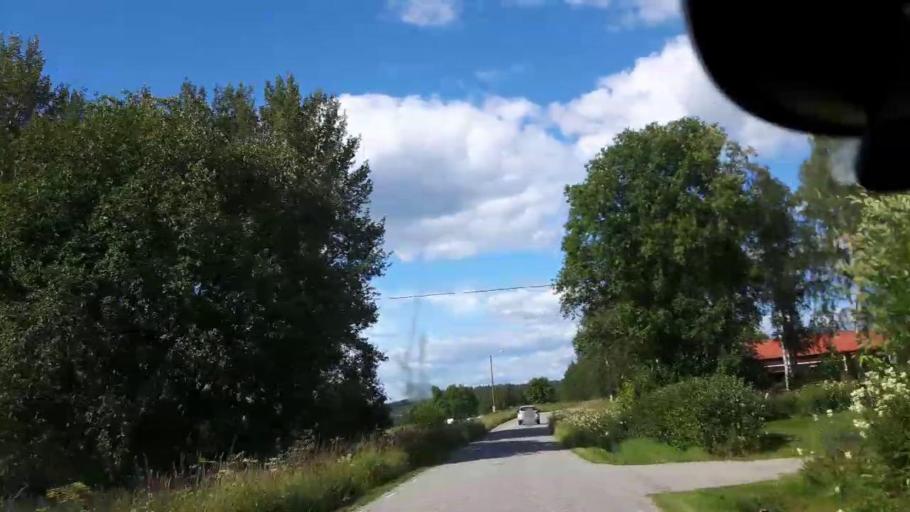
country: SE
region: Jaemtland
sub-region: Braecke Kommun
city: Braecke
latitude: 62.8759
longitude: 15.2730
